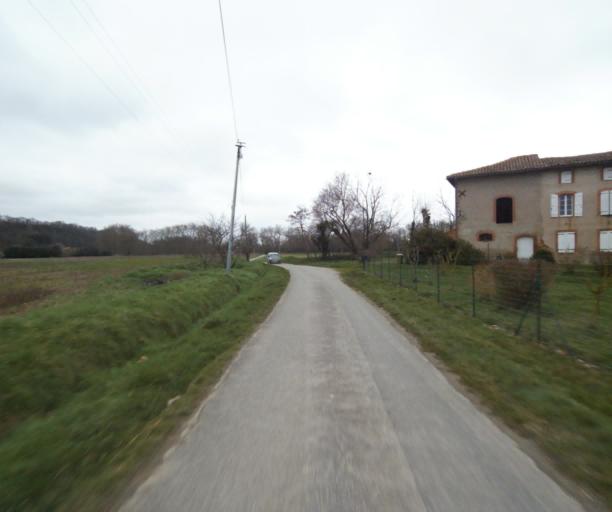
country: FR
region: Midi-Pyrenees
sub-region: Departement de l'Ariege
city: Saverdun
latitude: 43.2171
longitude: 1.5926
